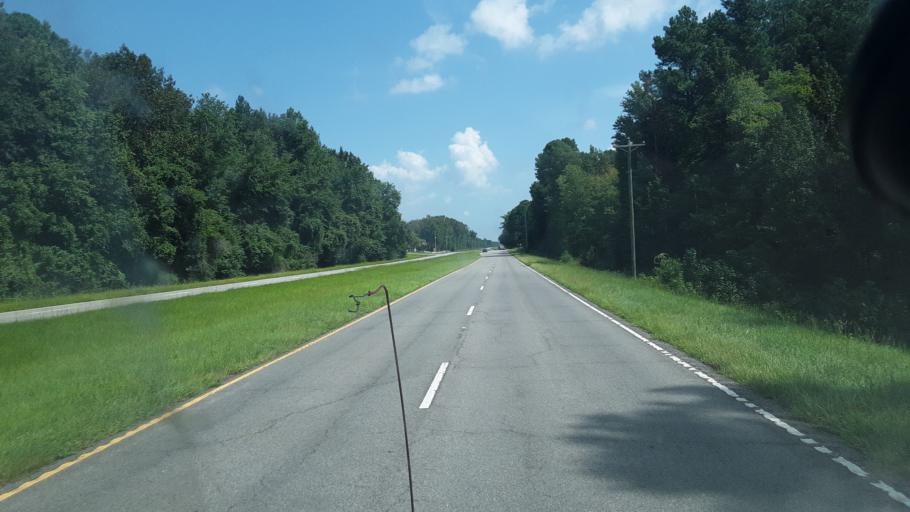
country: US
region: South Carolina
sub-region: Bamberg County
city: Bamberg
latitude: 33.3515
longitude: -81.0129
